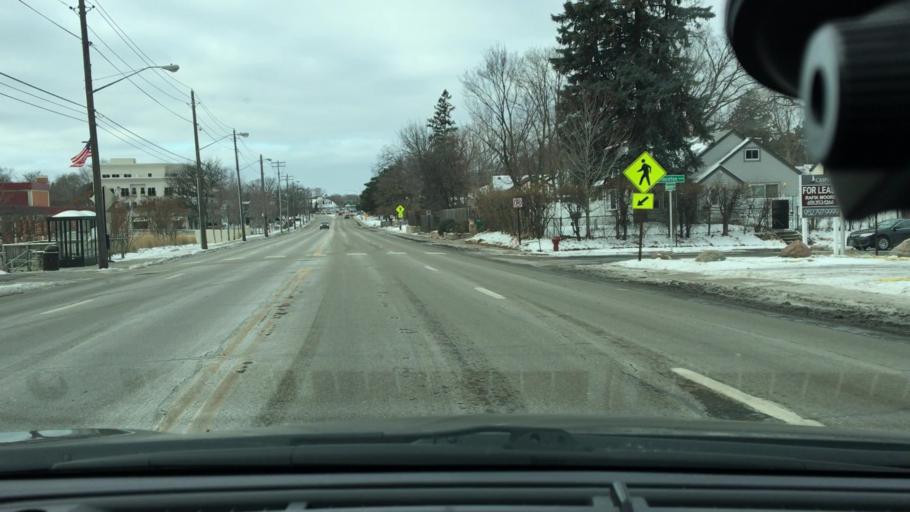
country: US
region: Minnesota
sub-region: Hennepin County
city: Saint Louis Park
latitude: 44.9485
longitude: -93.3413
